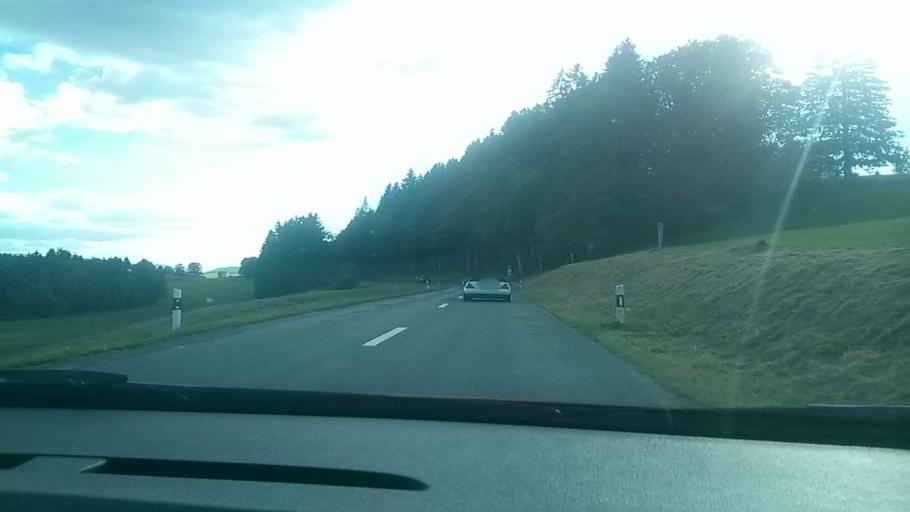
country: CH
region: Vaud
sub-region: Jura-Nord vaudois District
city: Le Chenit
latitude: 46.6303
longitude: 6.2490
